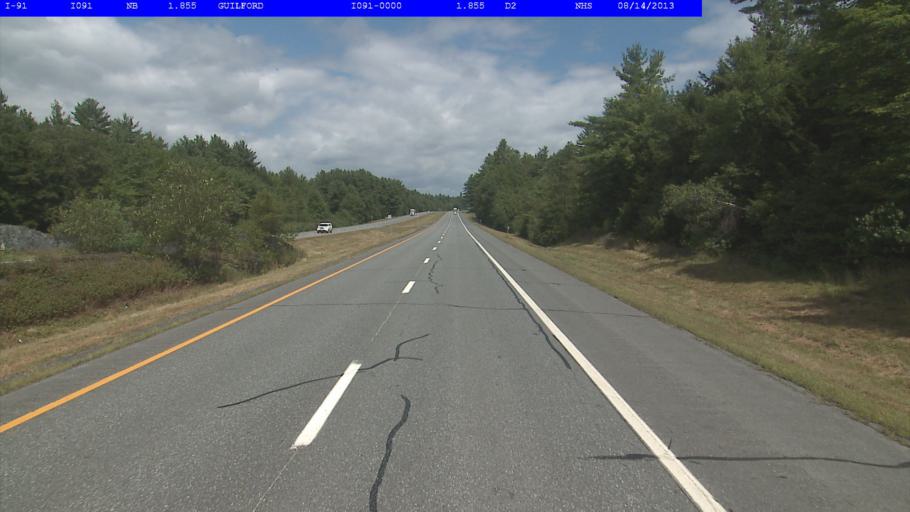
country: US
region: New Hampshire
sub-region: Cheshire County
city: Hinsdale
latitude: 42.7566
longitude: -72.5657
